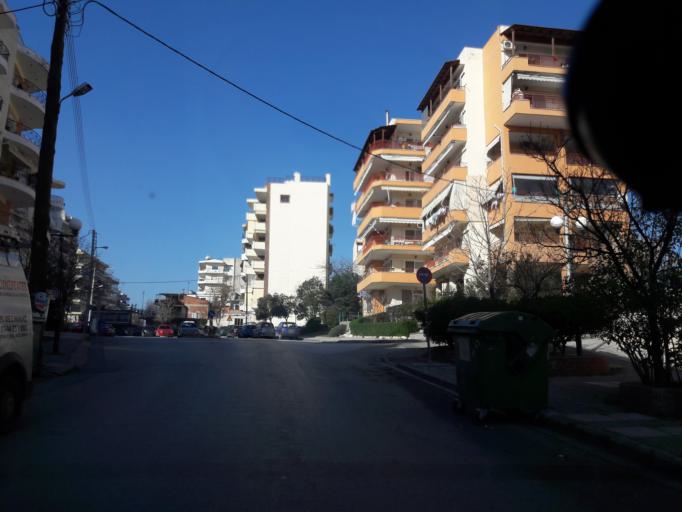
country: GR
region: Central Macedonia
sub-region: Nomos Thessalonikis
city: Stavroupoli
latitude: 40.6702
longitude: 22.9245
